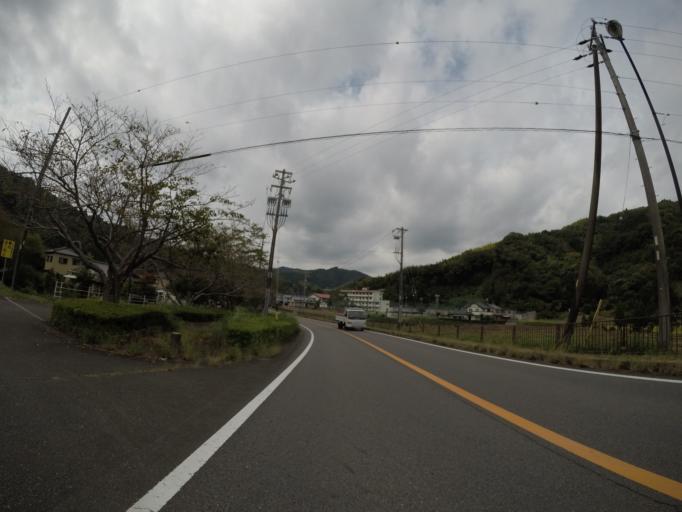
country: JP
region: Shizuoka
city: Fujieda
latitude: 34.8802
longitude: 138.2200
